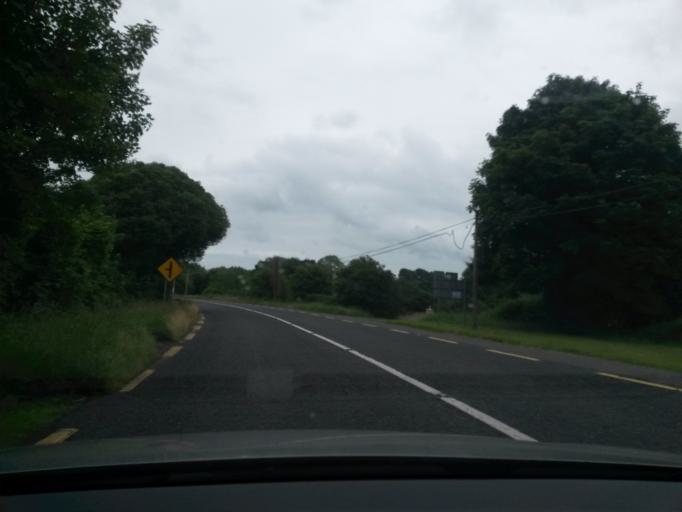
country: IE
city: Ballisodare
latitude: 54.2025
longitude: -8.5692
